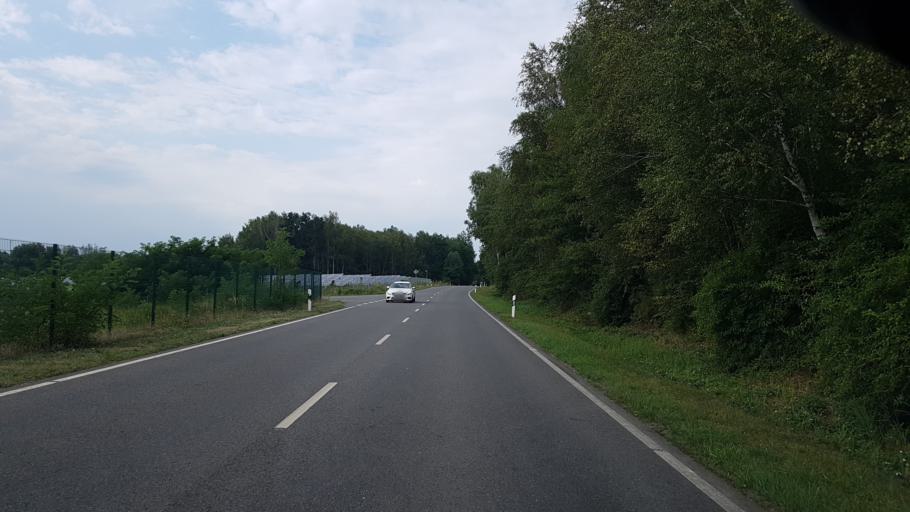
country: DE
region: Brandenburg
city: Lauchhammer
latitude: 51.4906
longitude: 13.7424
